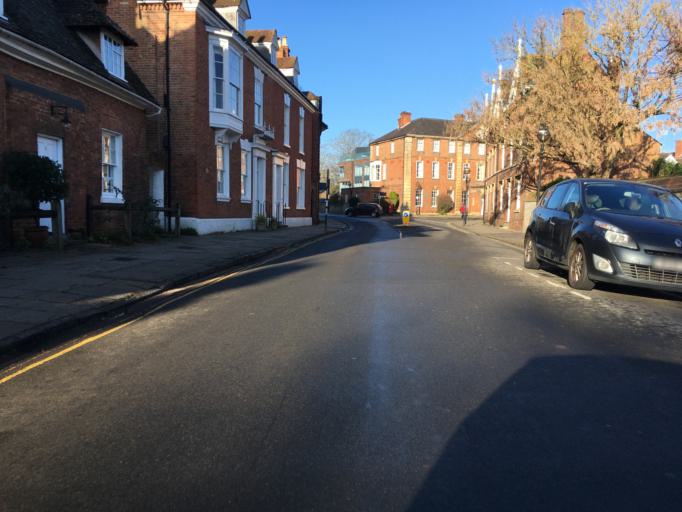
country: GB
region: England
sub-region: Warwickshire
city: Stratford-upon-Avon
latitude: 52.1888
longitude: -1.7091
